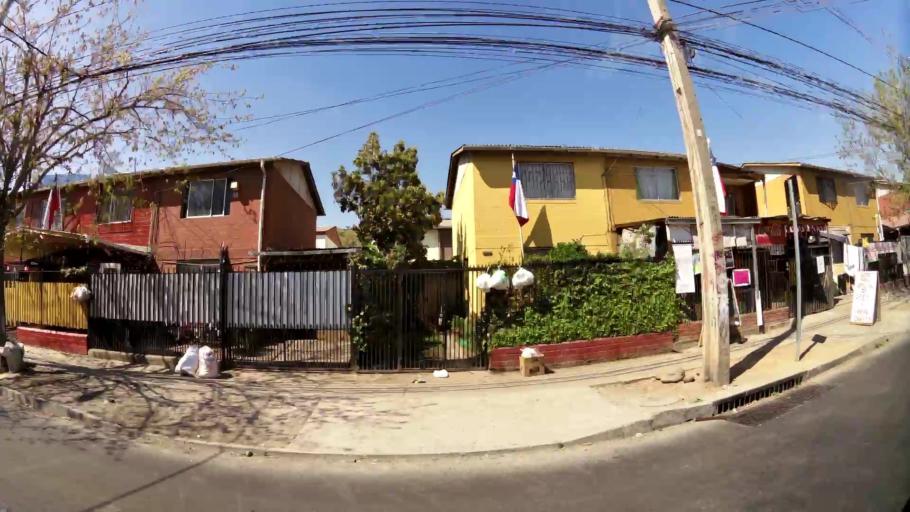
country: CL
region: Santiago Metropolitan
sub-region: Provincia de Cordillera
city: Puente Alto
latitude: -33.6248
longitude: -70.6075
